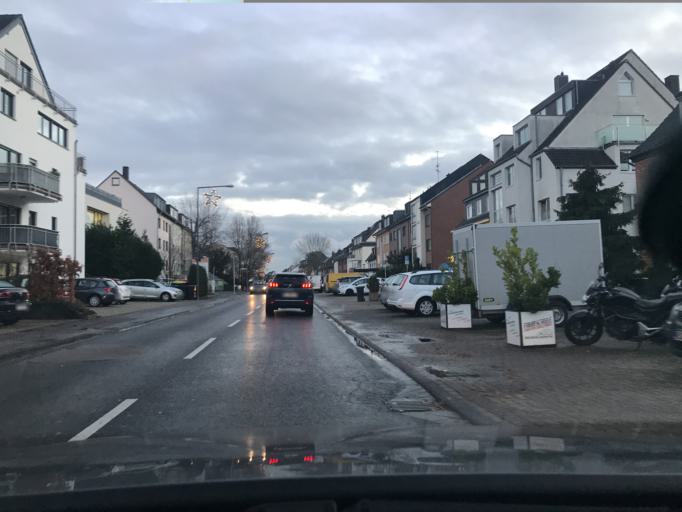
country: DE
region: North Rhine-Westphalia
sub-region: Regierungsbezirk Koln
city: Rath
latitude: 50.9488
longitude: 7.0793
